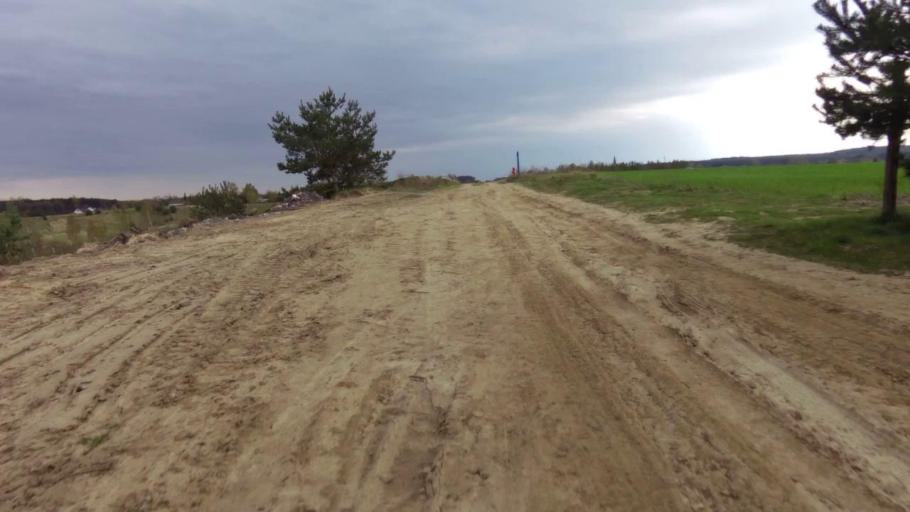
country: PL
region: West Pomeranian Voivodeship
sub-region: Powiat kamienski
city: Wolin
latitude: 53.9694
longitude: 14.6301
